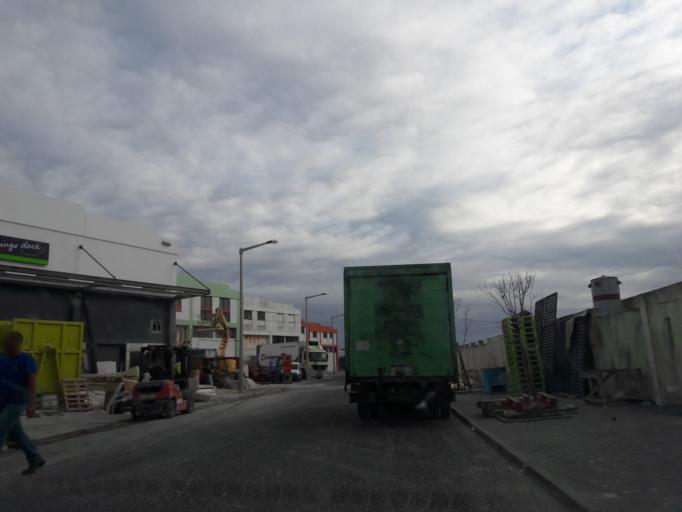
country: PT
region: Leiria
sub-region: Peniche
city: Peniche
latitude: 39.3596
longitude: -9.3749
